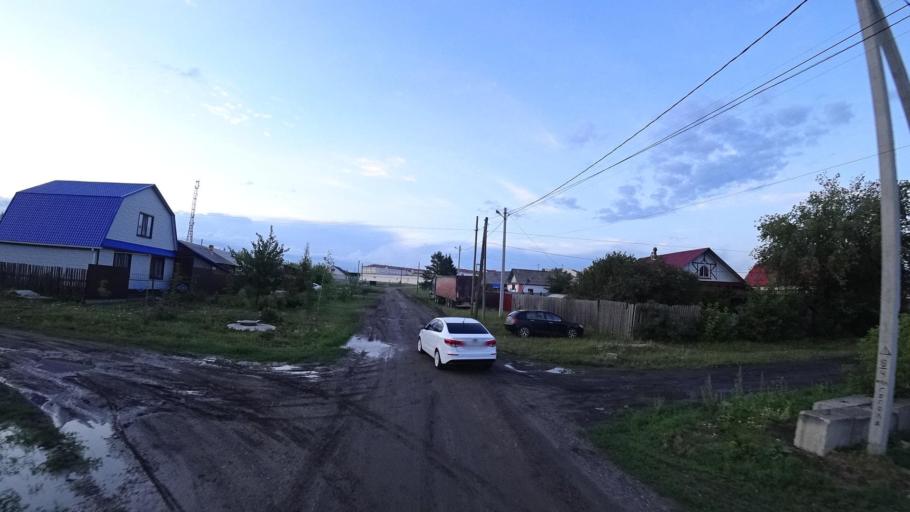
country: RU
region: Sverdlovsk
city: Kamyshlov
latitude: 56.8545
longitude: 62.7335
